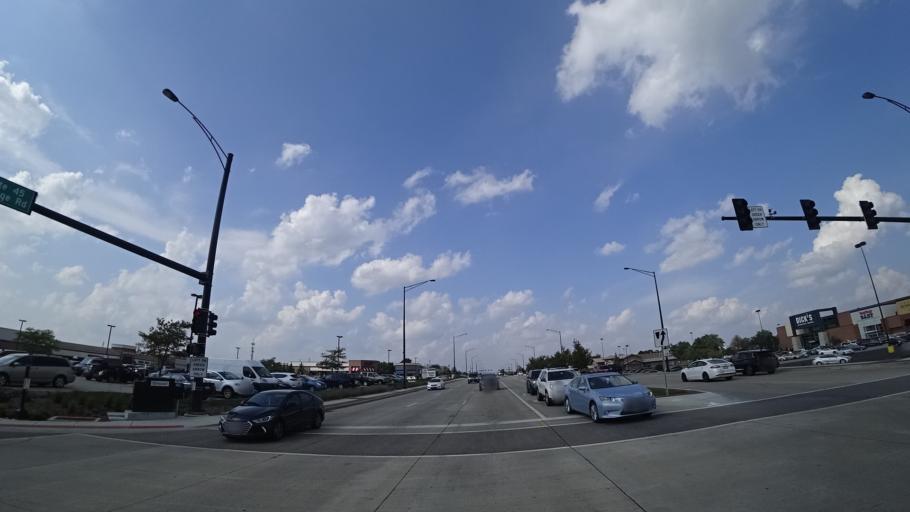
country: US
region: Illinois
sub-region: Cook County
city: Orland Park
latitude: 41.6123
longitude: -87.8534
